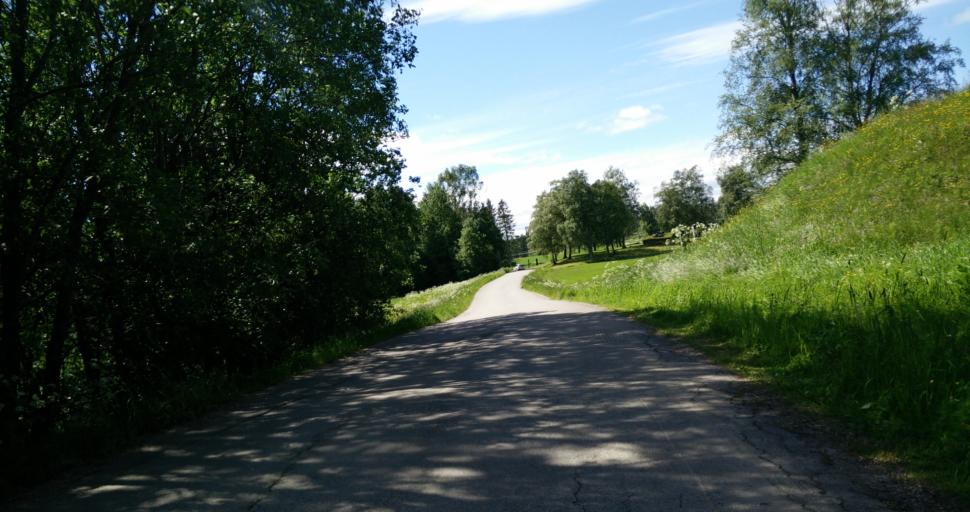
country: SE
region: Vaesternorrland
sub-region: Sundsvalls Kommun
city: Nolby
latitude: 62.2852
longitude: 17.3672
